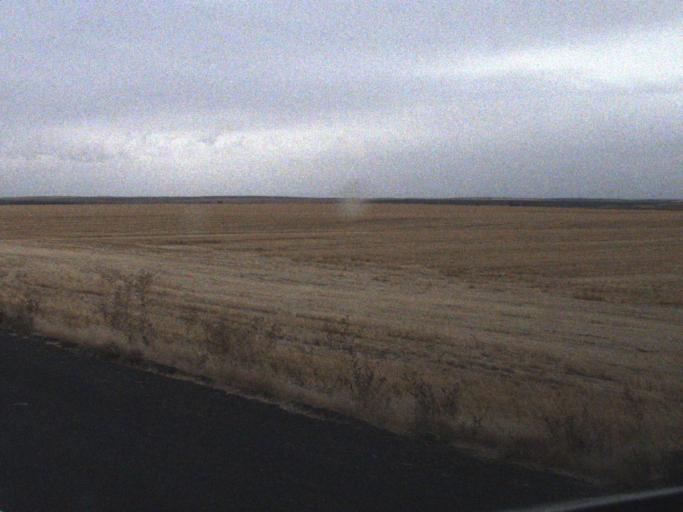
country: US
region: Washington
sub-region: Franklin County
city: Connell
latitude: 46.7945
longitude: -118.6042
